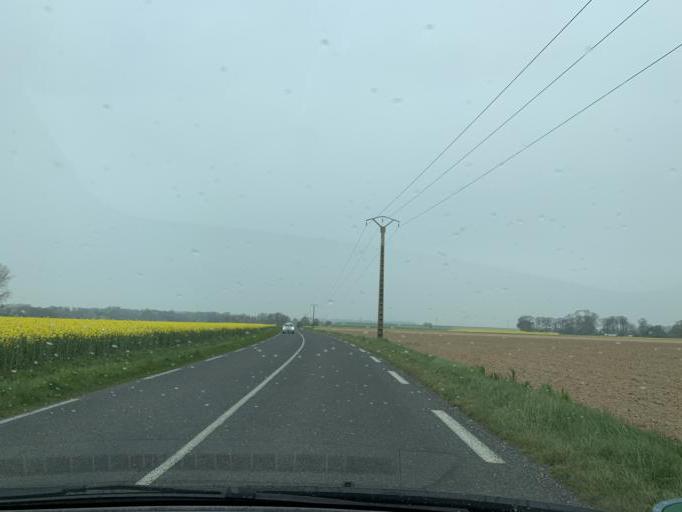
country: FR
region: Haute-Normandie
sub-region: Departement de la Seine-Maritime
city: Cany-Barville
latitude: 49.7958
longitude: 0.6637
